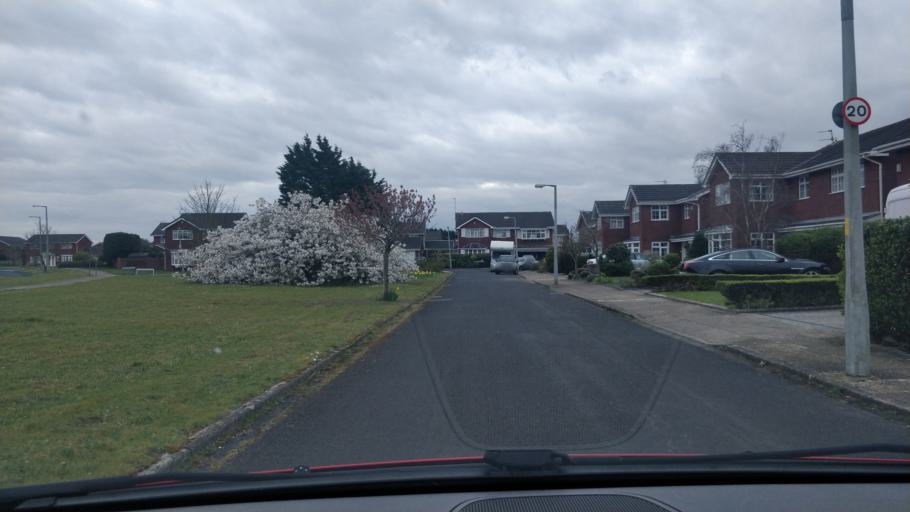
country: GB
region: England
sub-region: Sefton
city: Formby
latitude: 53.6014
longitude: -3.0504
